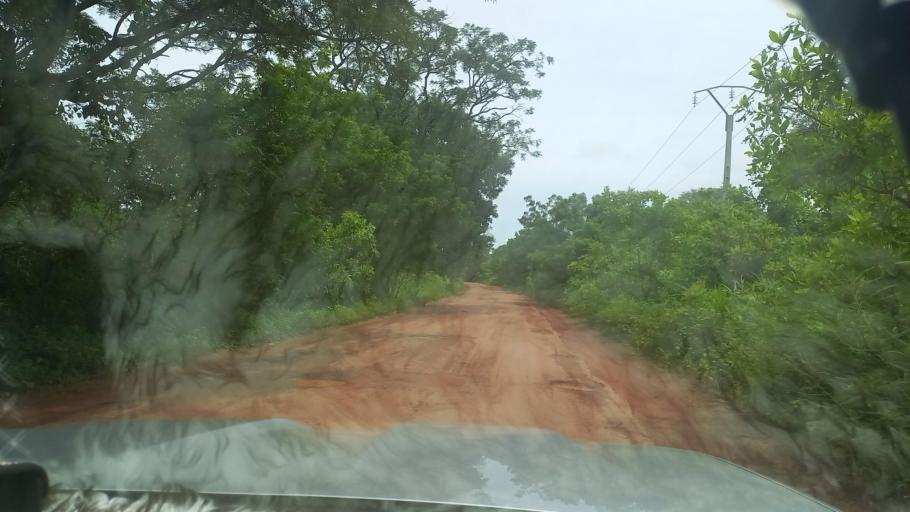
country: SN
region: Kolda
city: Marsassoum
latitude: 12.9053
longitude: -16.0172
